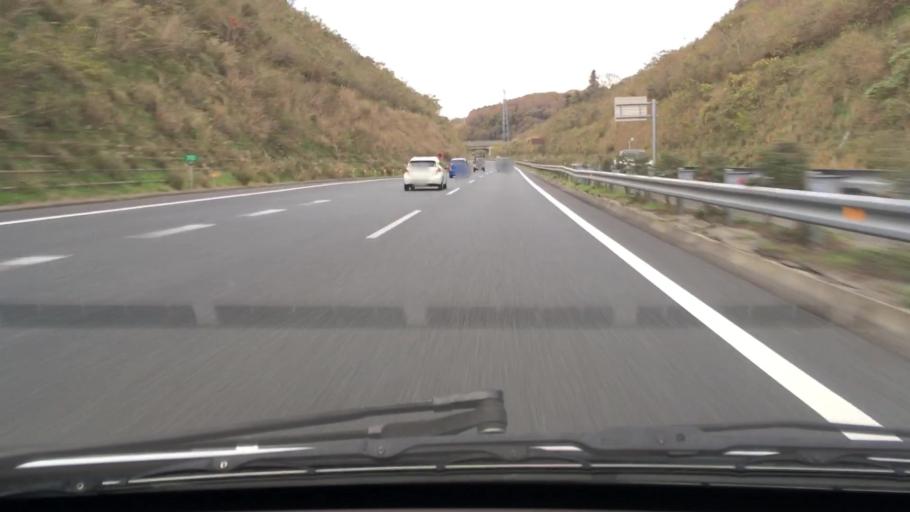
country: JP
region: Chiba
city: Kimitsu
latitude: 35.3222
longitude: 139.9449
